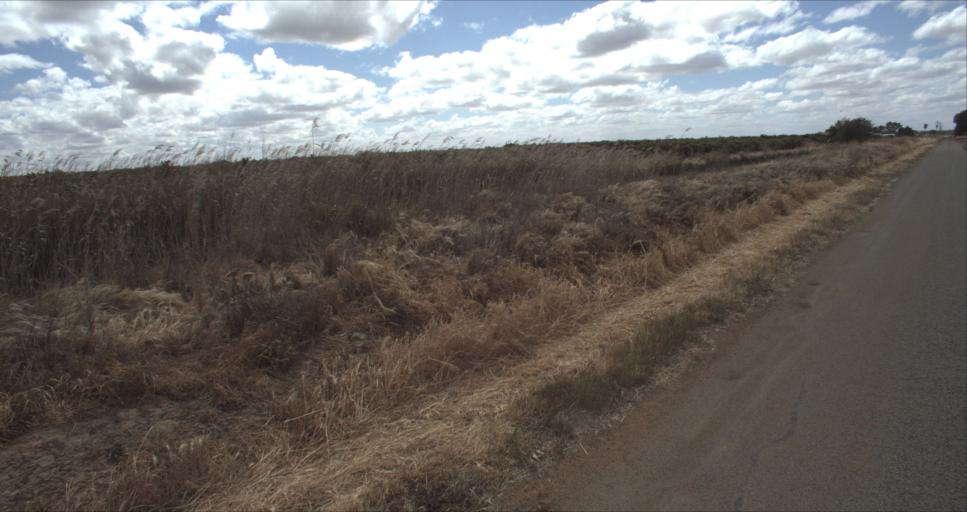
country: AU
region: New South Wales
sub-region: Leeton
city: Leeton
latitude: -34.5882
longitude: 146.3909
